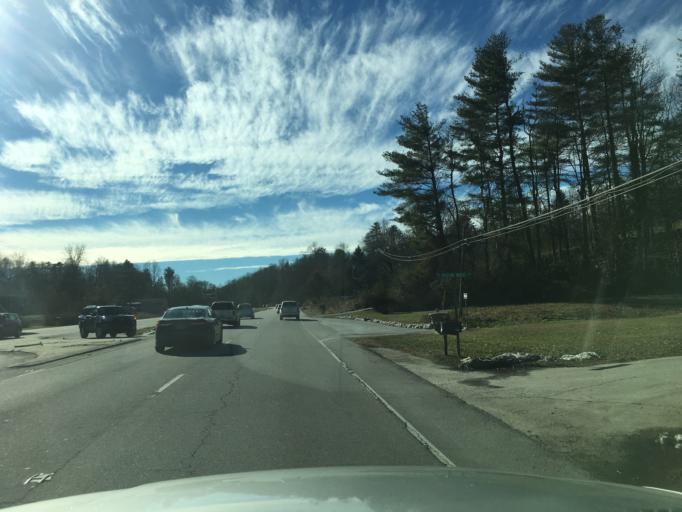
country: US
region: North Carolina
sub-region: Transylvania County
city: Brevard
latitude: 35.2699
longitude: -82.7091
